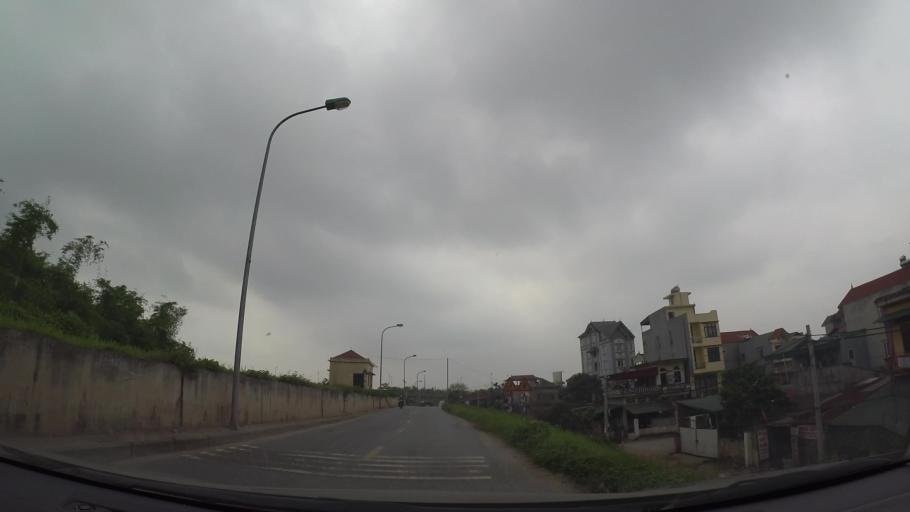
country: VN
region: Ha Noi
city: Trau Quy
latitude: 21.0397
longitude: 105.9351
